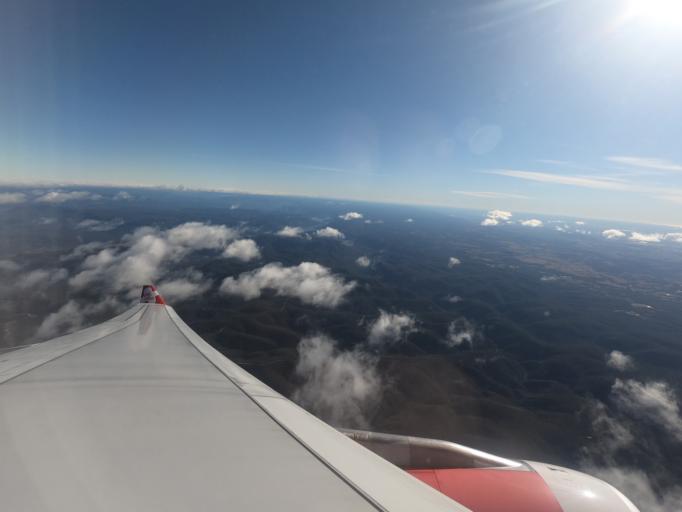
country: AU
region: New South Wales
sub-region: Wollondilly
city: Buxton
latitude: -34.2705
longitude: 150.4378
